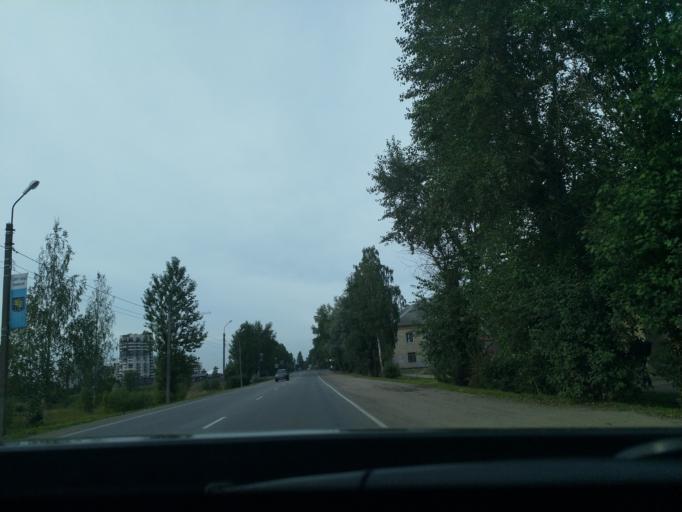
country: RU
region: Leningrad
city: Nikol'skoye
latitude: 59.7030
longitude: 30.7846
